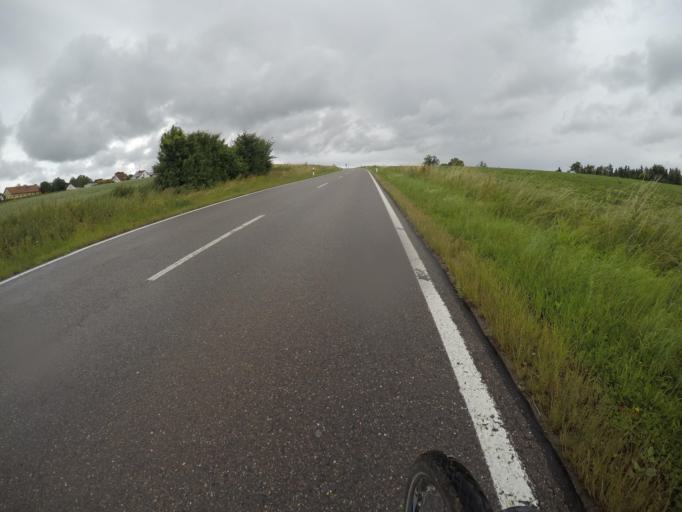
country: DE
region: Baden-Wuerttemberg
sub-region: Regierungsbezirk Stuttgart
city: Unterjettingen
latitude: 48.5696
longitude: 8.8153
